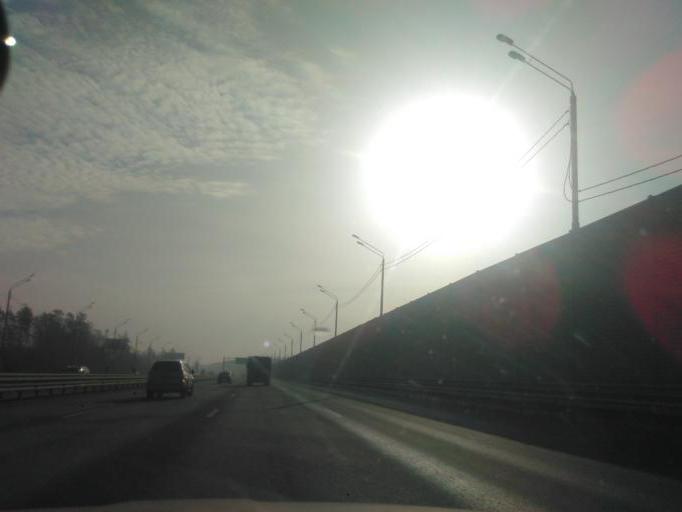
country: RU
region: Moskovskaya
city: Petrovo-Dal'neye
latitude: 55.7838
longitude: 37.1465
